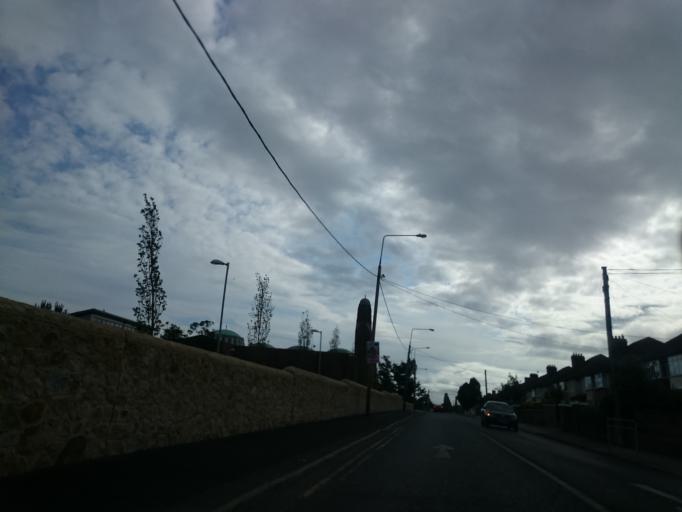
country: IE
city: Milltown
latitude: 53.3052
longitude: -6.2454
